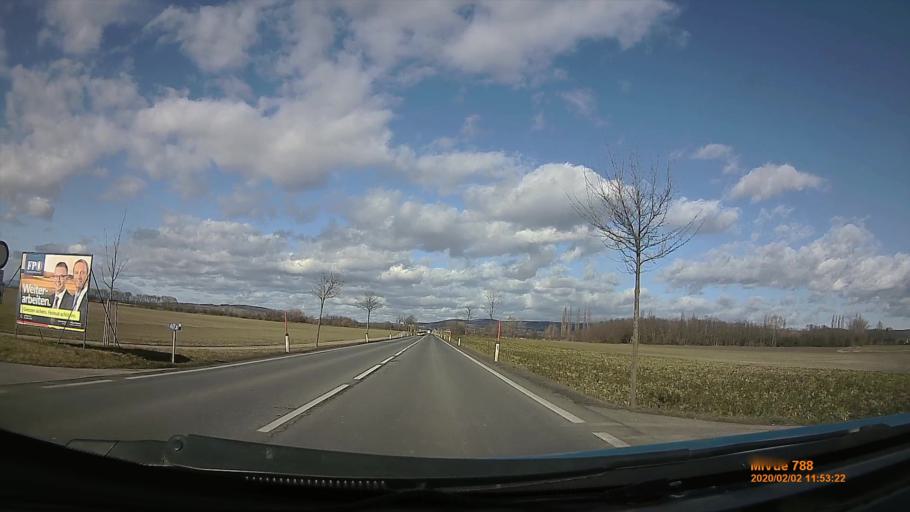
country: AT
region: Burgenland
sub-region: Eisenstadt-Umgebung
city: Zagersdorf
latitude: 47.7834
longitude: 16.5194
